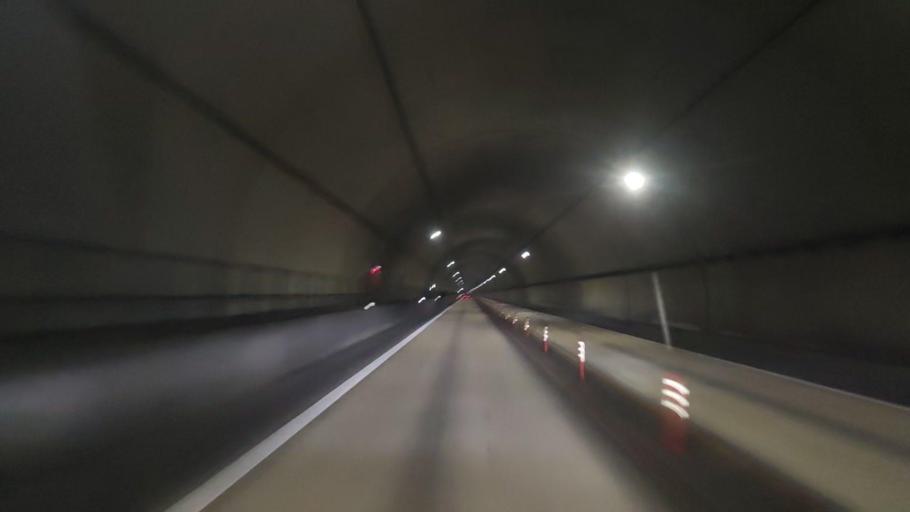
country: JP
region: Wakayama
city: Tanabe
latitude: 33.5703
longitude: 135.4840
